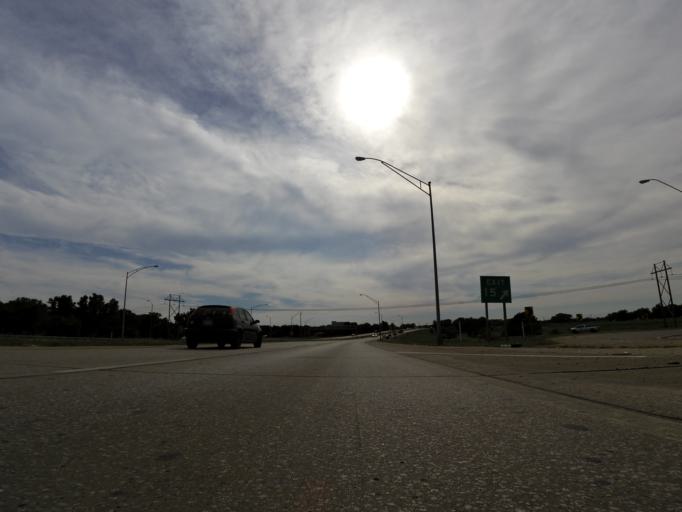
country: US
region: Kansas
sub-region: Sedgwick County
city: Park City
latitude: 37.7570
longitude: -97.3382
